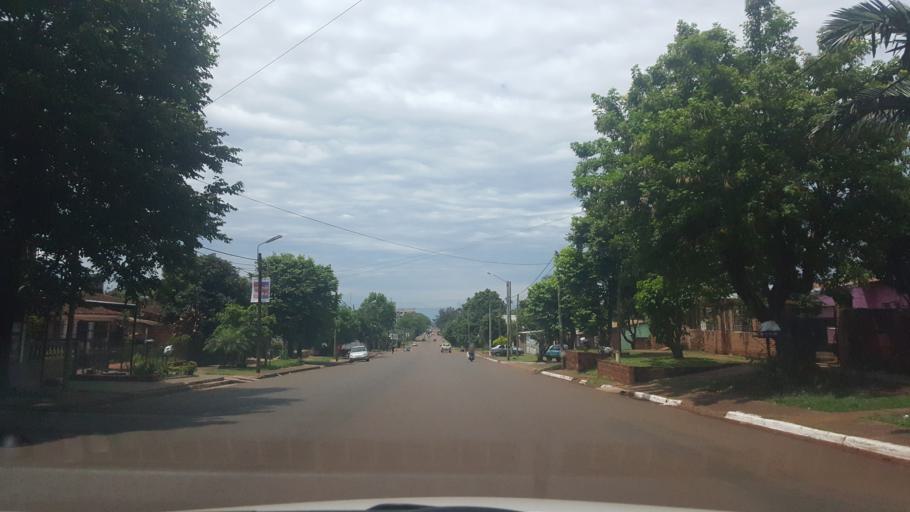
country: AR
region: Misiones
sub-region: Departamento de Capital
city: Posadas
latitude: -27.3784
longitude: -55.9232
